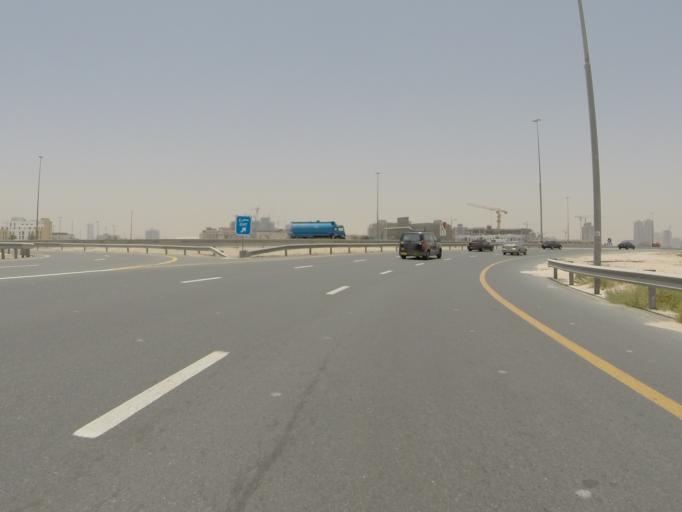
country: AE
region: Dubai
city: Dubai
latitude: 25.0641
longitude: 55.1977
